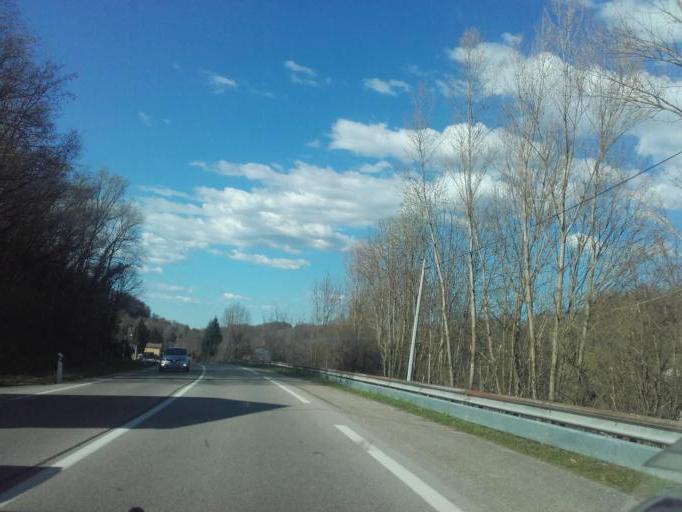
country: FR
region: Rhone-Alpes
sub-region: Departement de l'Isere
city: Nivolas-Vermelle
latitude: 45.5349
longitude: 5.3102
